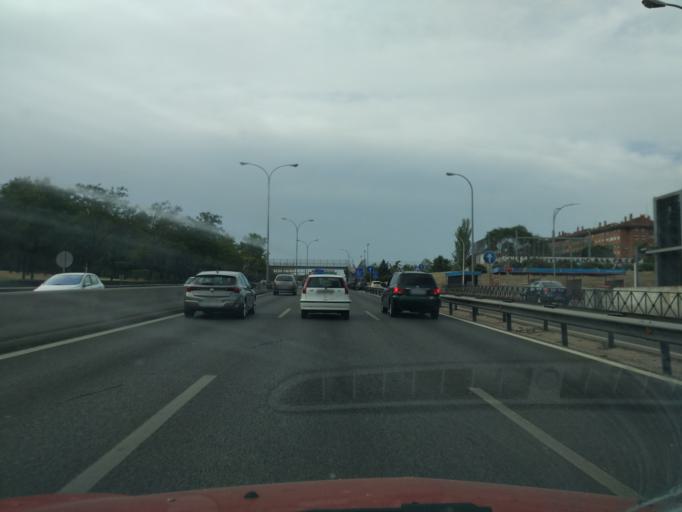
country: ES
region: Madrid
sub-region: Provincia de Madrid
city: Carabanchel
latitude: 40.3786
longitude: -3.7190
